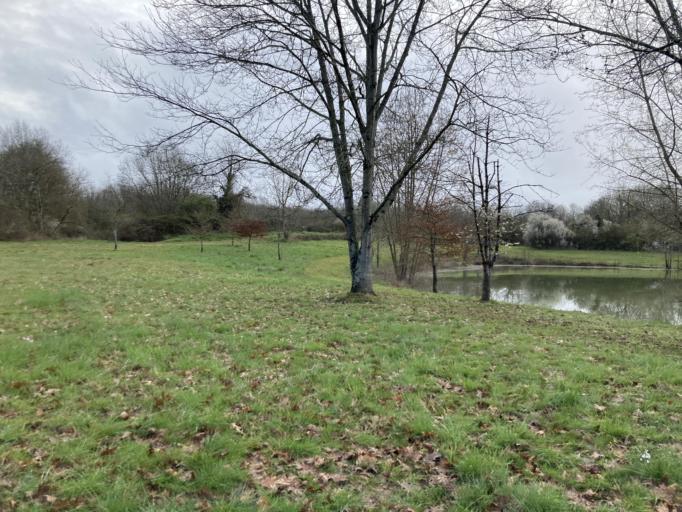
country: FR
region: Aquitaine
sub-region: Departement des Landes
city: Souprosse
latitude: 43.7629
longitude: -0.6862
